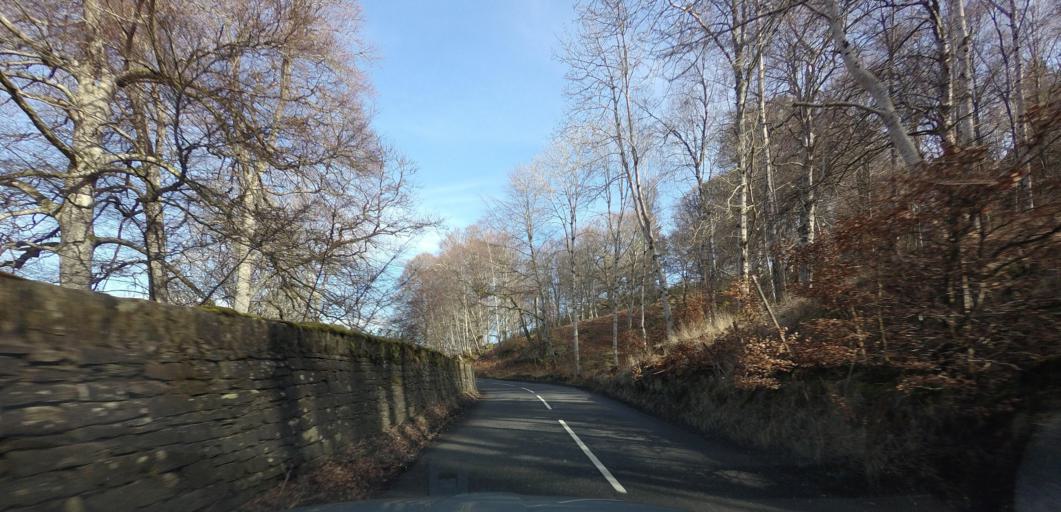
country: GB
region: Scotland
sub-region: Perth and Kinross
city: Aberfeldy
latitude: 56.5855
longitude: -3.9805
